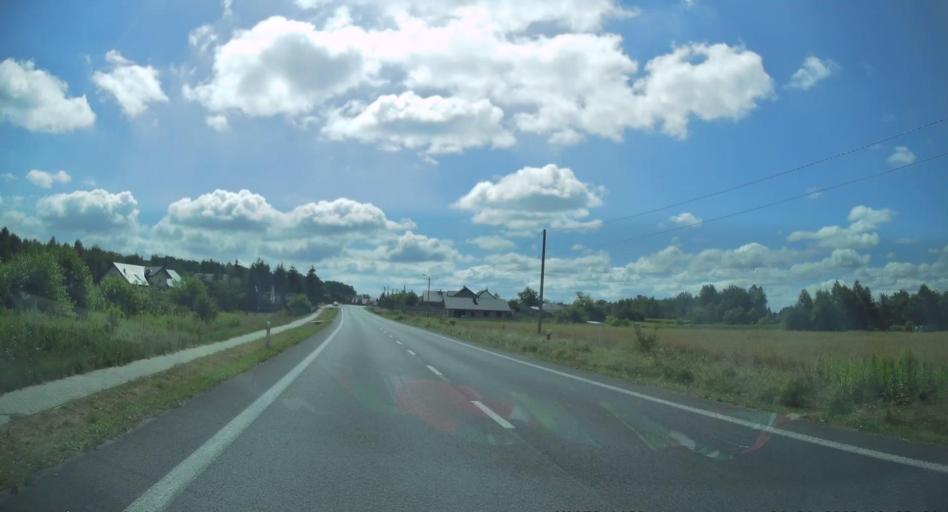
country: PL
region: Subcarpathian Voivodeship
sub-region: Powiat debicki
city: Brzeznica
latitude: 50.1238
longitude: 21.4870
